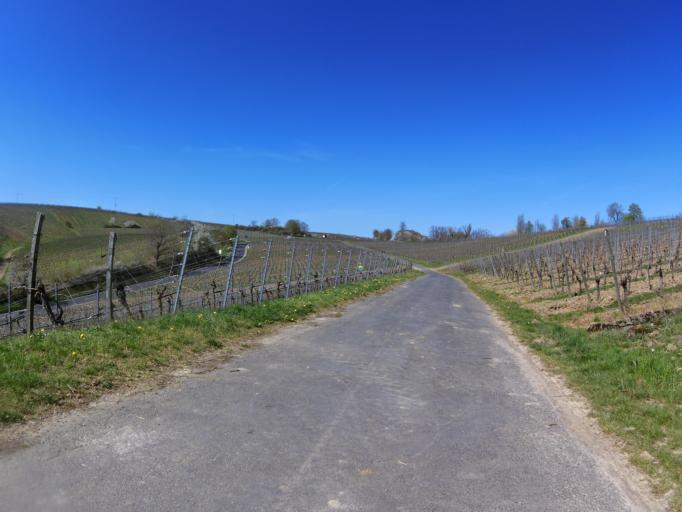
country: DE
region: Bavaria
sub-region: Regierungsbezirk Unterfranken
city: Nordheim
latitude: 49.8649
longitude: 10.1711
